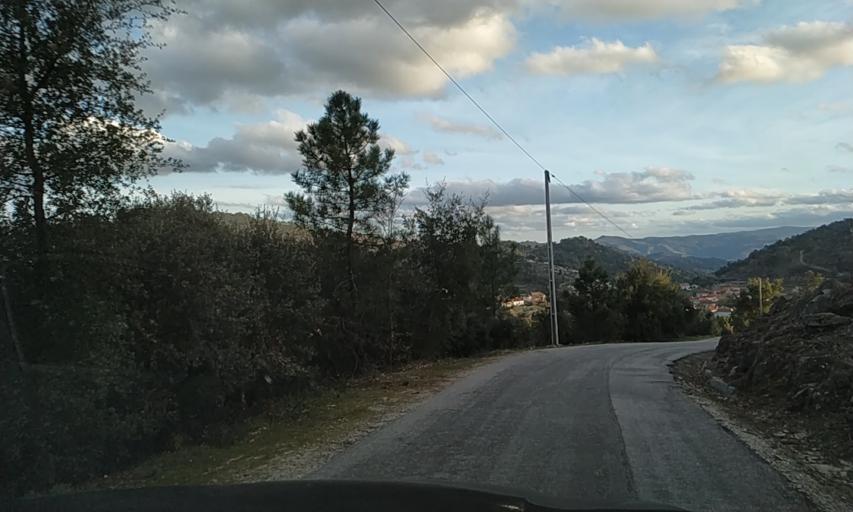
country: PT
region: Braganca
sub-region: Carrazeda de Ansiaes
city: Carrazeda de Anciaes
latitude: 41.2124
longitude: -7.3634
